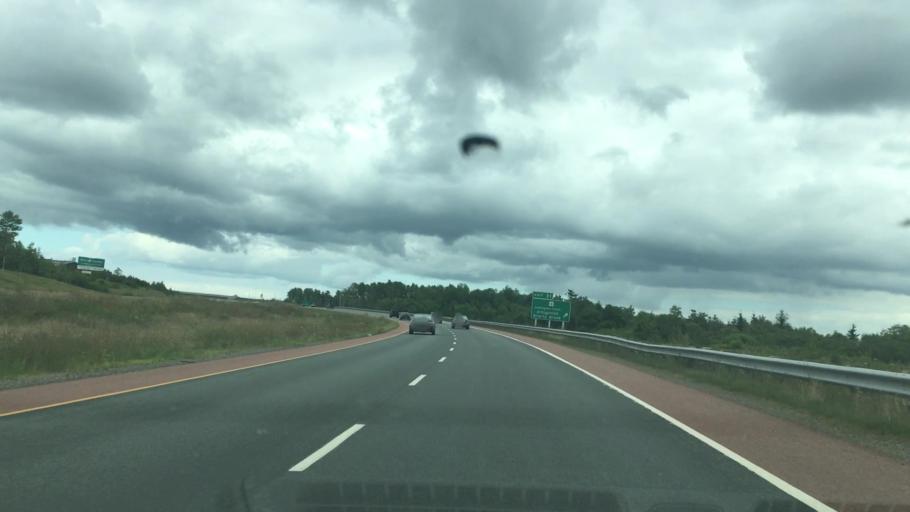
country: CA
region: Nova Scotia
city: Antigonish
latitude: 45.5977
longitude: -62.0322
